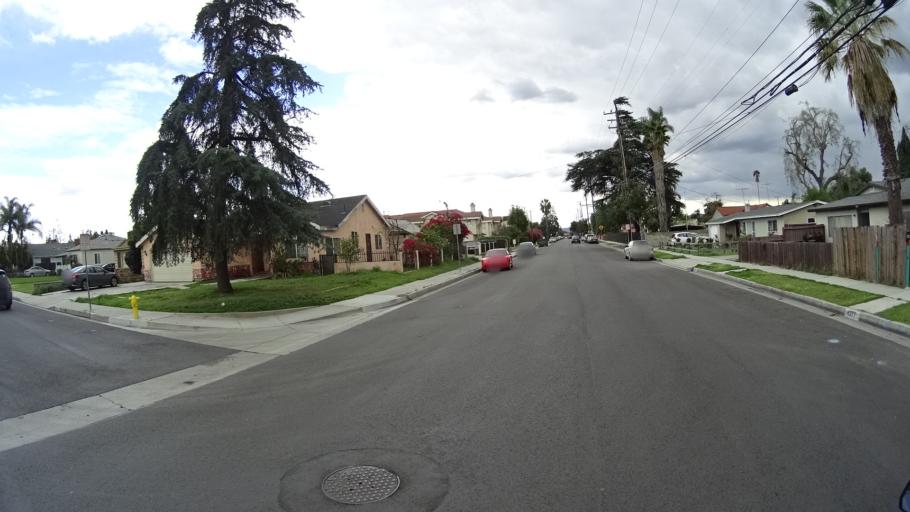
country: US
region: California
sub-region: Los Angeles County
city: Baldwin Park
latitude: 34.0904
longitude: -117.9671
